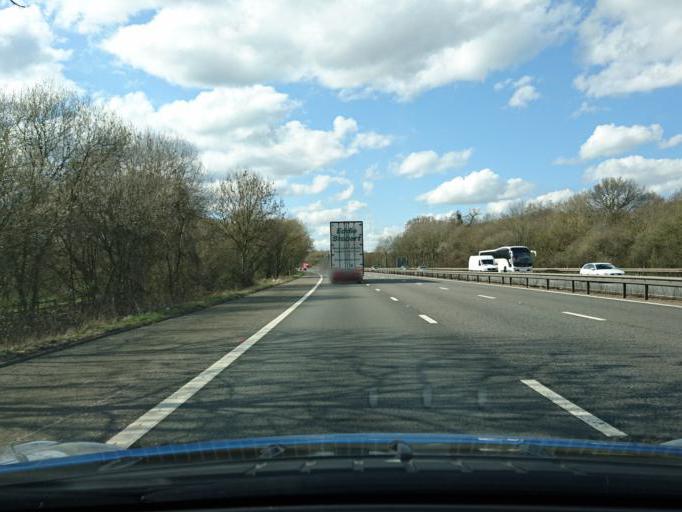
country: GB
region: England
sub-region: West Berkshire
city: Theale
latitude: 51.4537
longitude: -1.0814
